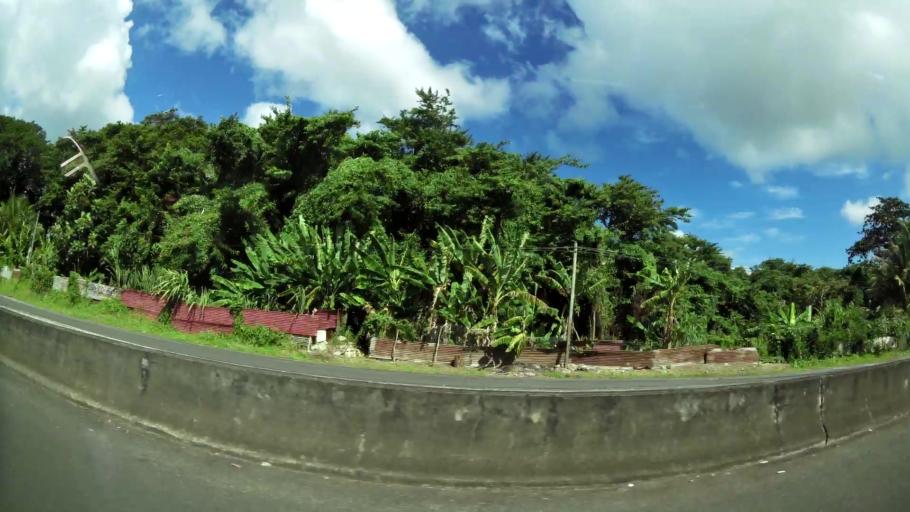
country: GP
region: Guadeloupe
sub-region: Guadeloupe
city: Pointe-a-Pitre
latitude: 16.2541
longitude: -61.5404
